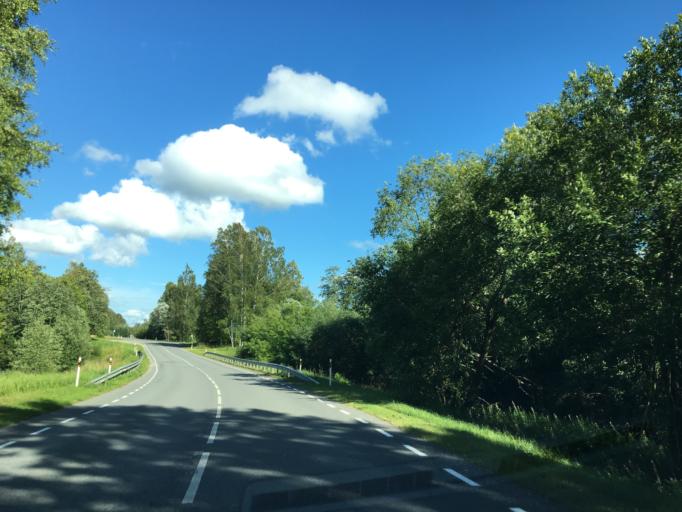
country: EE
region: Paernumaa
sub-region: Vaendra vald (alev)
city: Vandra
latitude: 58.5745
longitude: 25.1984
